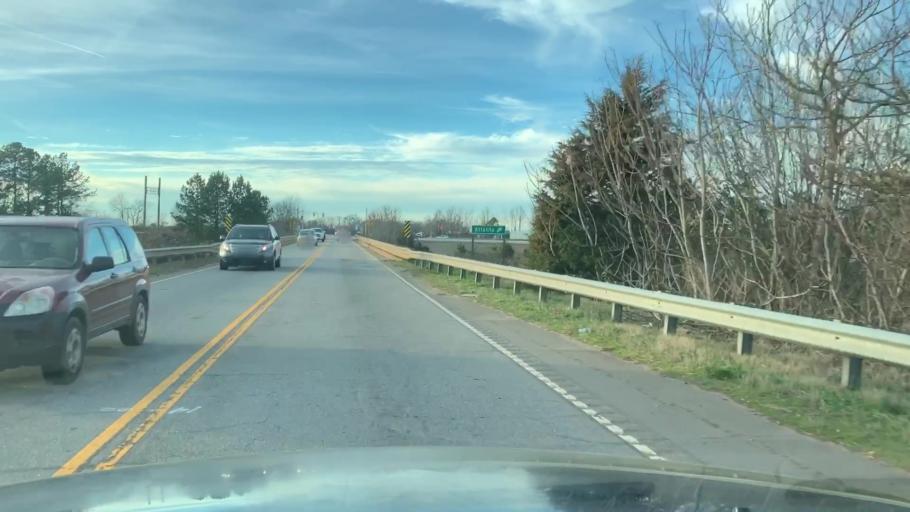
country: US
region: Georgia
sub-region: Hart County
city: Reed Creek
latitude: 34.5267
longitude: -82.8427
